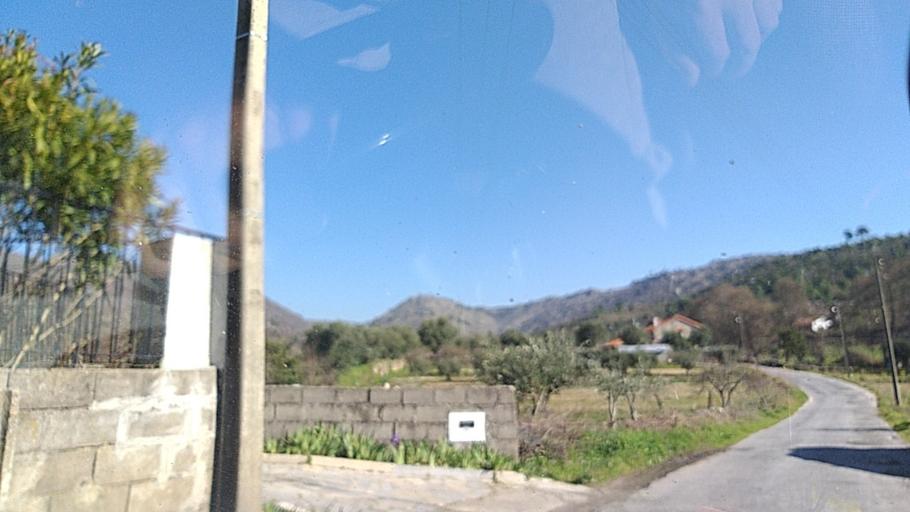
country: PT
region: Guarda
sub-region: Celorico da Beira
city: Celorico da Beira
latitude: 40.6864
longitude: -7.4030
